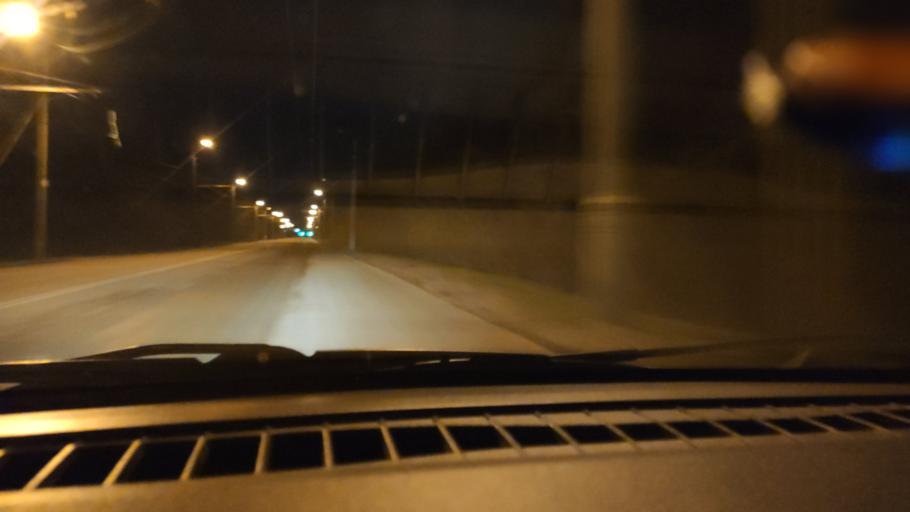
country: RU
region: Bashkortostan
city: Sterlitamak
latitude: 53.6574
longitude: 55.9219
